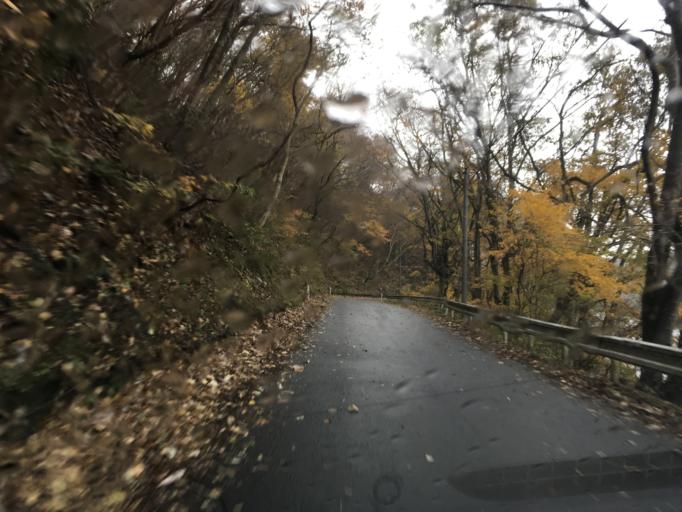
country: JP
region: Iwate
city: Ichinoseki
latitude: 38.8134
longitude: 141.2525
